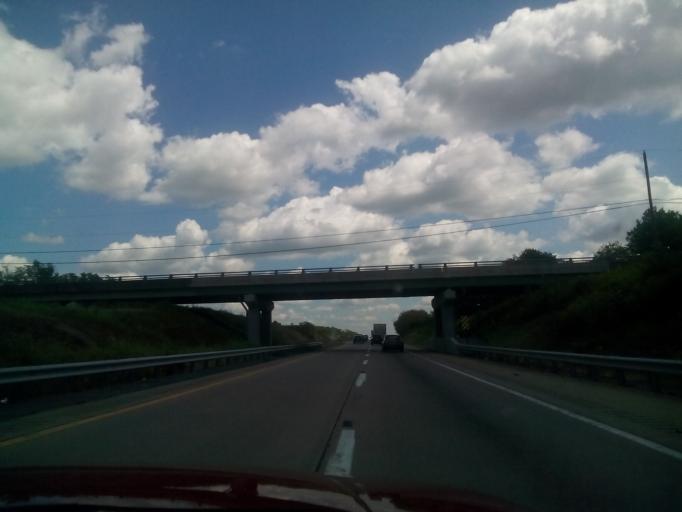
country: US
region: Pennsylvania
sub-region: Northumberland County
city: Riverside
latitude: 40.9867
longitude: -76.7077
